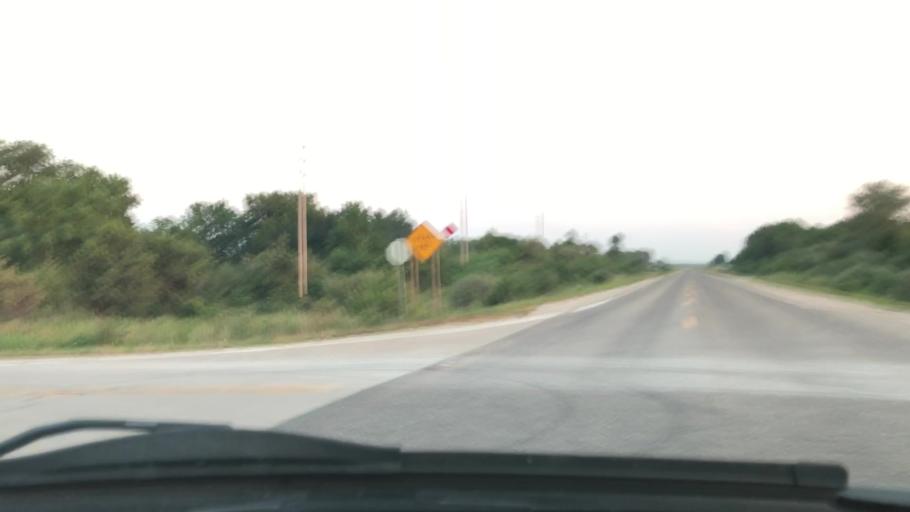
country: US
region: Iowa
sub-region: Henry County
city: Mount Pleasant
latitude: 40.9377
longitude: -91.5400
